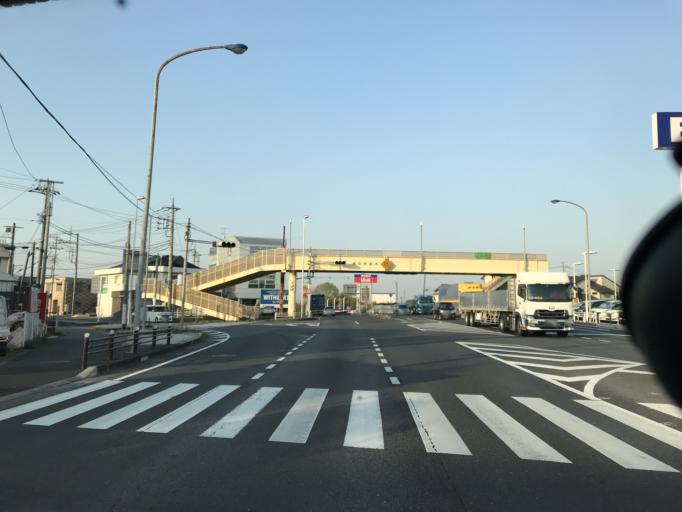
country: JP
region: Chiba
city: Narita
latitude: 35.7608
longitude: 140.3050
